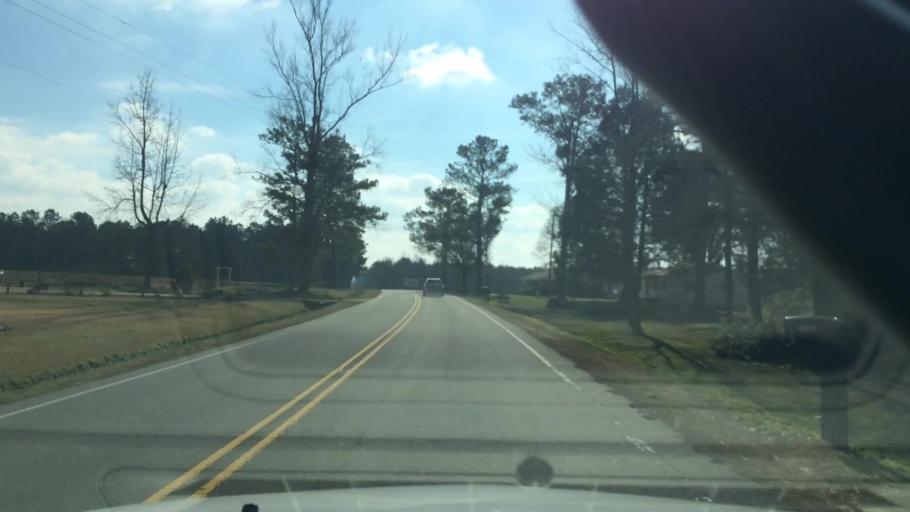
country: US
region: North Carolina
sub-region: Duplin County
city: Beulaville
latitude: 34.8552
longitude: -77.7978
